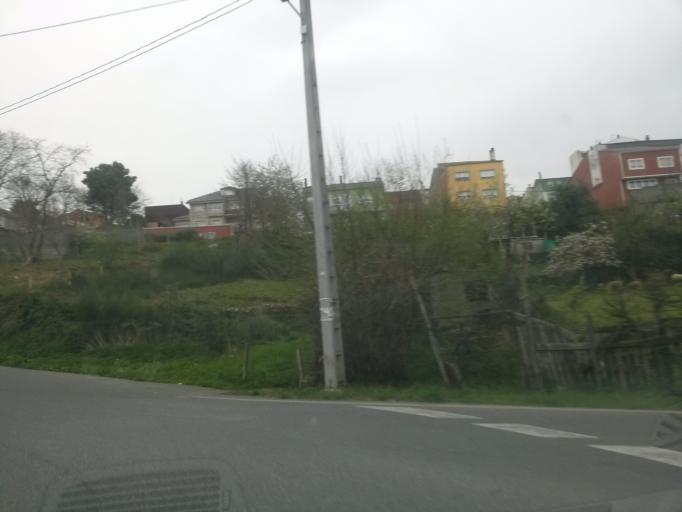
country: ES
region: Galicia
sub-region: Provincia de Lugo
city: Lugo
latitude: 43.0227
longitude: -7.5553
